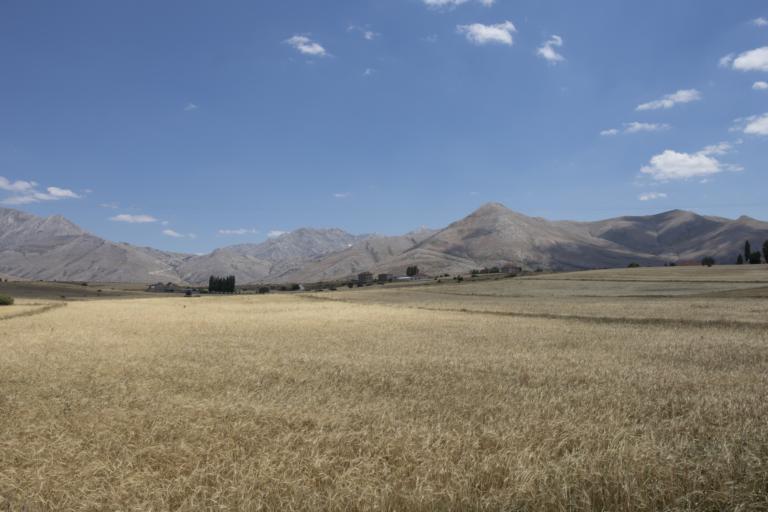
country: TR
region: Kayseri
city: Toklar
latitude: 38.4136
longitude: 36.0792
